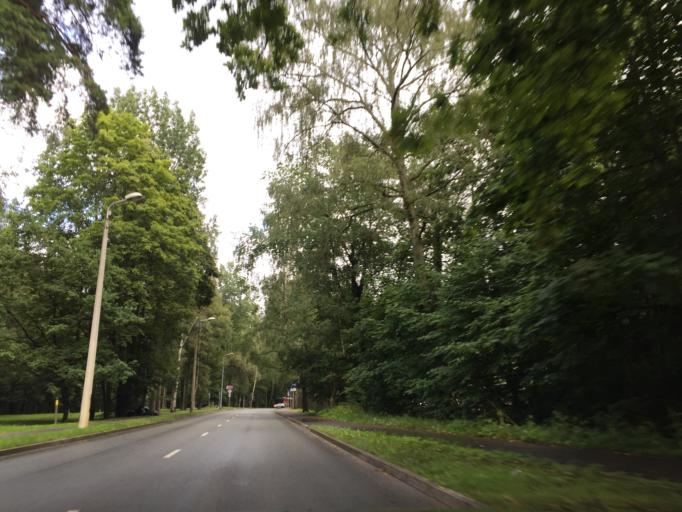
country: LV
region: Marupe
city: Marupe
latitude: 56.9535
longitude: 24.0121
